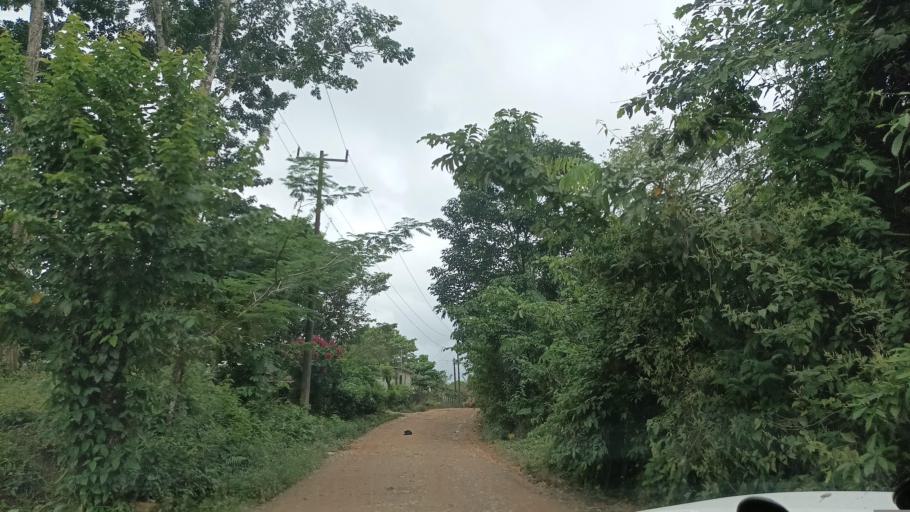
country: MX
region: Veracruz
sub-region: Uxpanapa
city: Poblado 10
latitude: 17.2709
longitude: -94.4963
